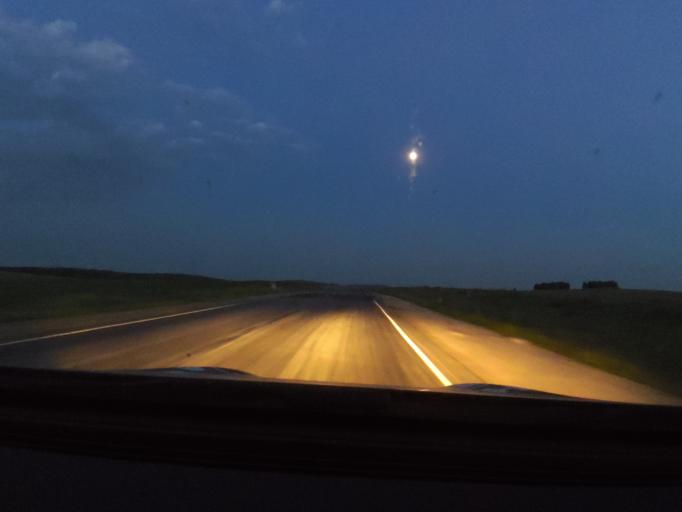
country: RU
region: Bashkortostan
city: Duvan
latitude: 55.9370
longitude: 58.2002
